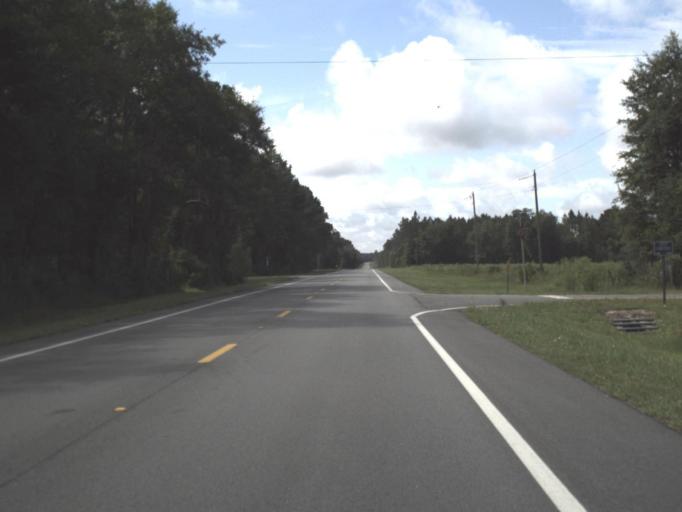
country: US
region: Florida
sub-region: Columbia County
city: Five Points
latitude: 30.3785
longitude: -82.6245
